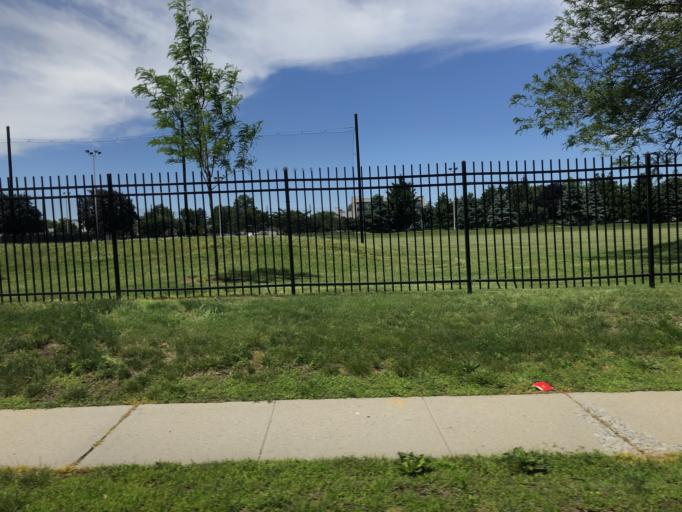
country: US
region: New York
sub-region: Nassau County
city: Uniondale
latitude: 40.7139
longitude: -73.5935
